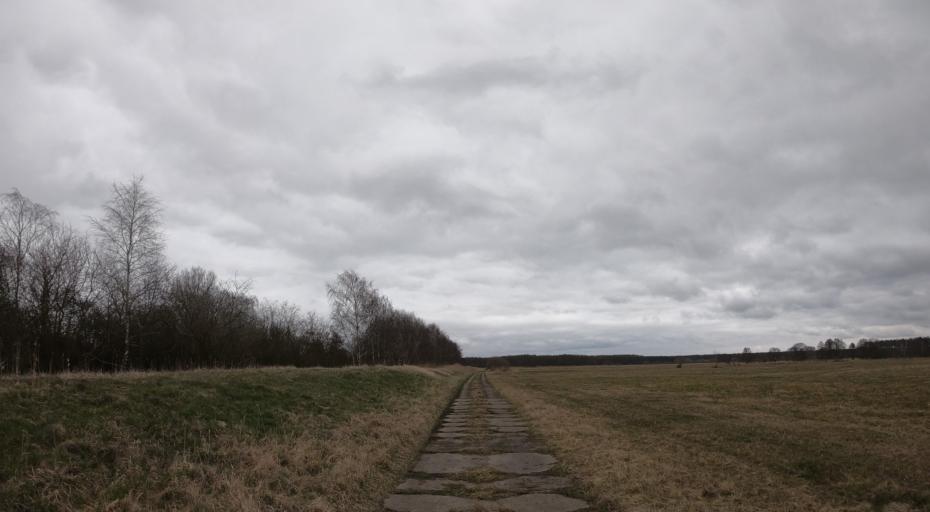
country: PL
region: West Pomeranian Voivodeship
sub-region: Powiat policki
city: Nowe Warpno
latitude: 53.6890
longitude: 14.3853
